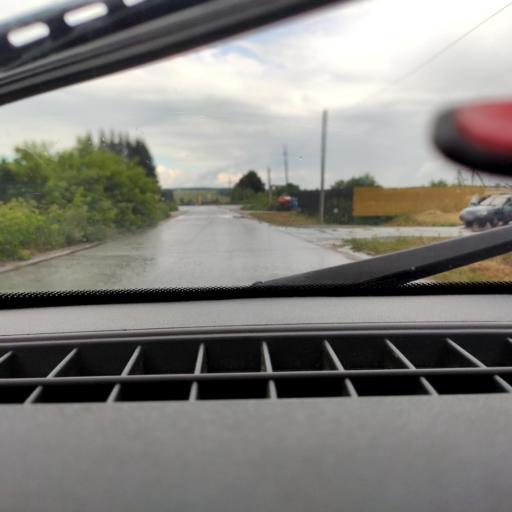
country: RU
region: Bashkortostan
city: Kabakovo
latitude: 54.5804
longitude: 56.2785
